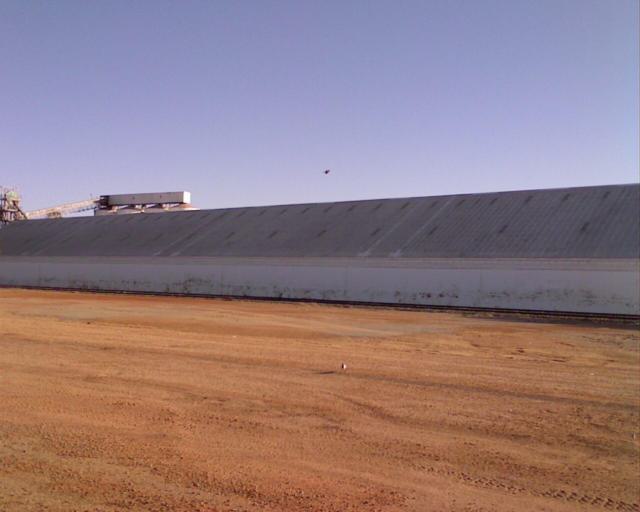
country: AU
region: Western Australia
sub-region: Wongan-Ballidu
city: Wongan Hills
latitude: -30.3625
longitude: 117.1174
